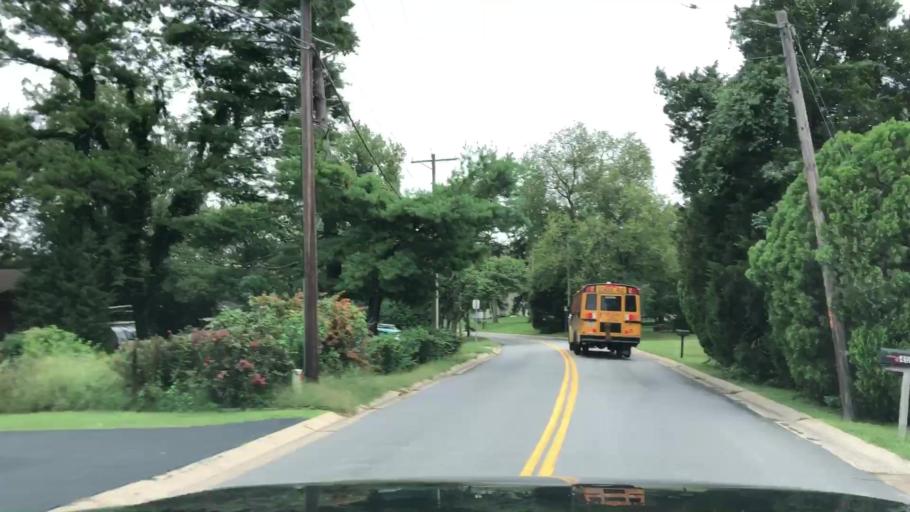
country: US
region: Missouri
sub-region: Saint Louis County
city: Manchester
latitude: 38.5861
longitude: -90.5104
